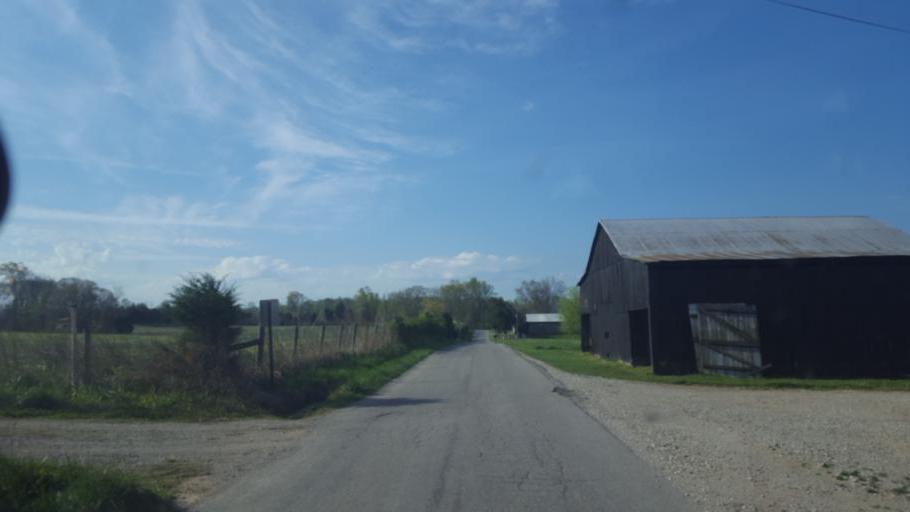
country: US
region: Kentucky
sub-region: Hart County
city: Munfordville
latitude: 37.3291
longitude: -86.0795
